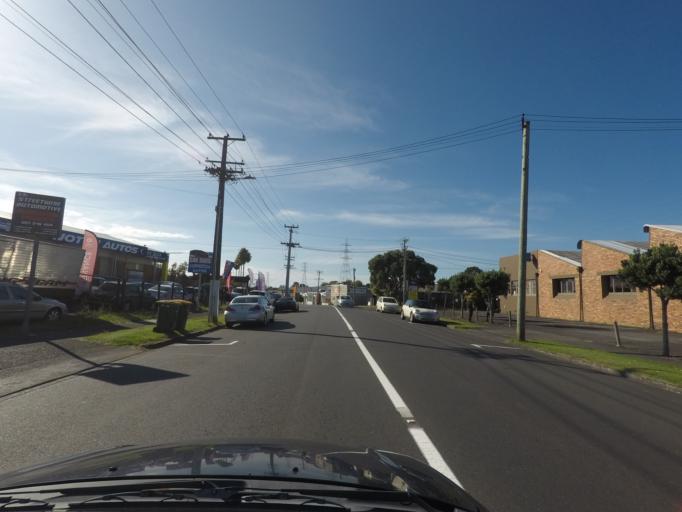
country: NZ
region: Auckland
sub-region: Auckland
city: Waitakere
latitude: -36.9059
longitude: 174.6904
